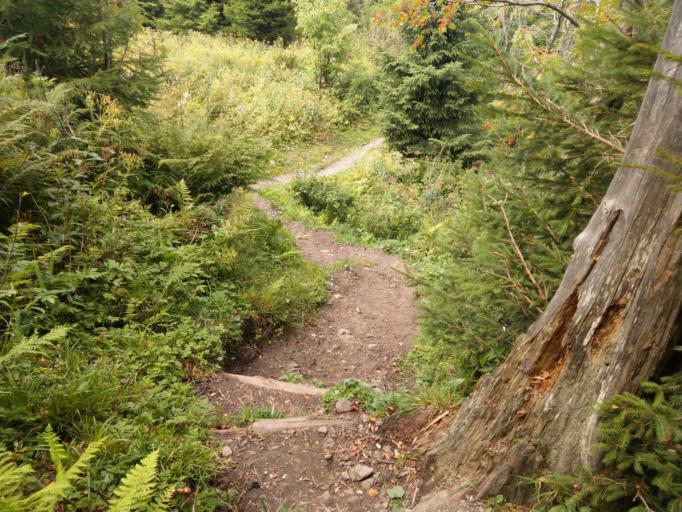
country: DE
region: Bavaria
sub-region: Swabia
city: Nesselwang
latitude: 47.6027
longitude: 10.5013
